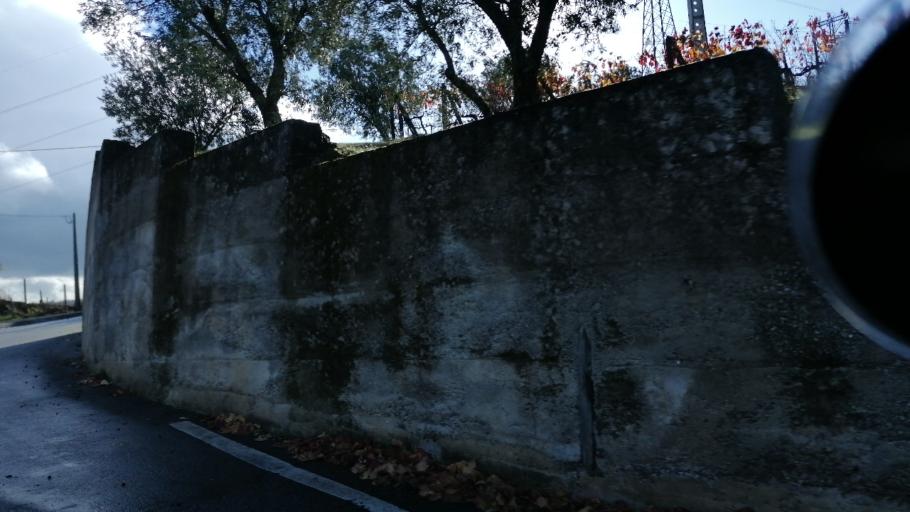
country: PT
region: Viseu
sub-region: Lamego
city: Lamego
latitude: 41.1180
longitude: -7.7894
